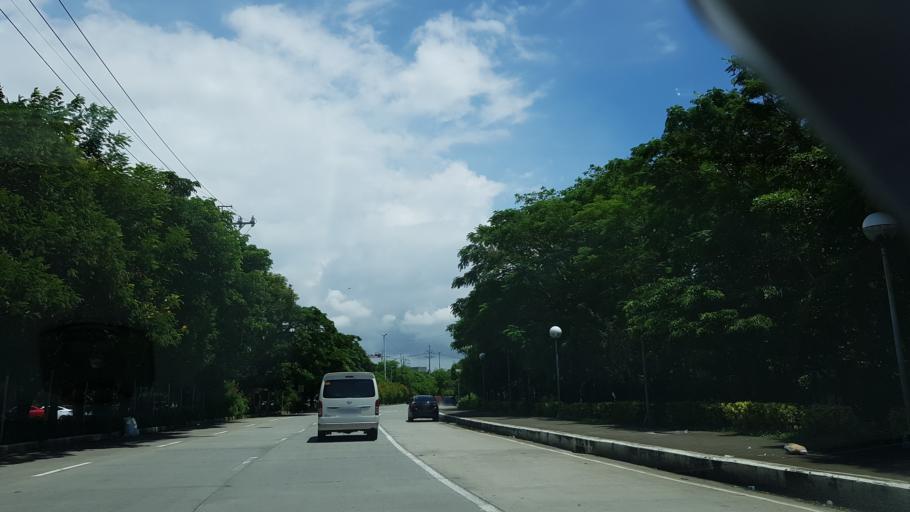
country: PH
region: Metro Manila
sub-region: City of Manila
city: Port Area
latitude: 14.5477
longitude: 120.9821
